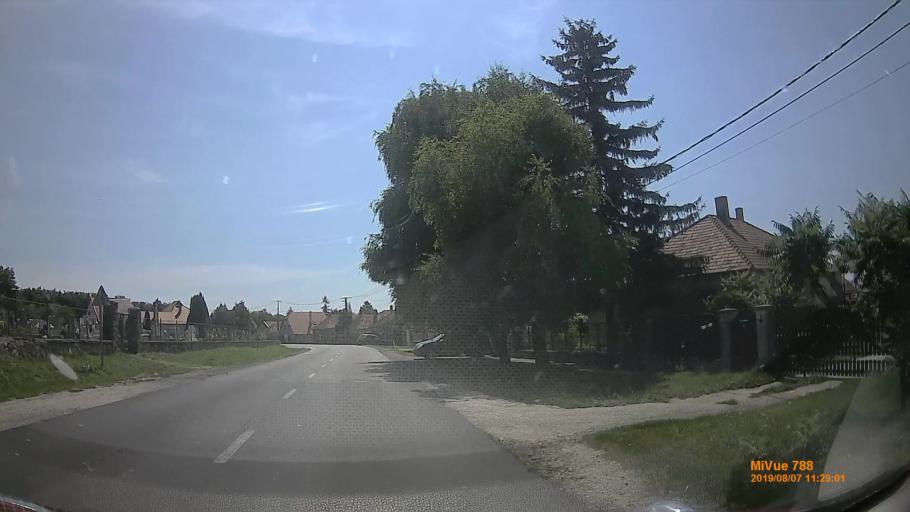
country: HU
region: Veszprem
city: Tapolca
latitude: 46.9176
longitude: 17.4528
